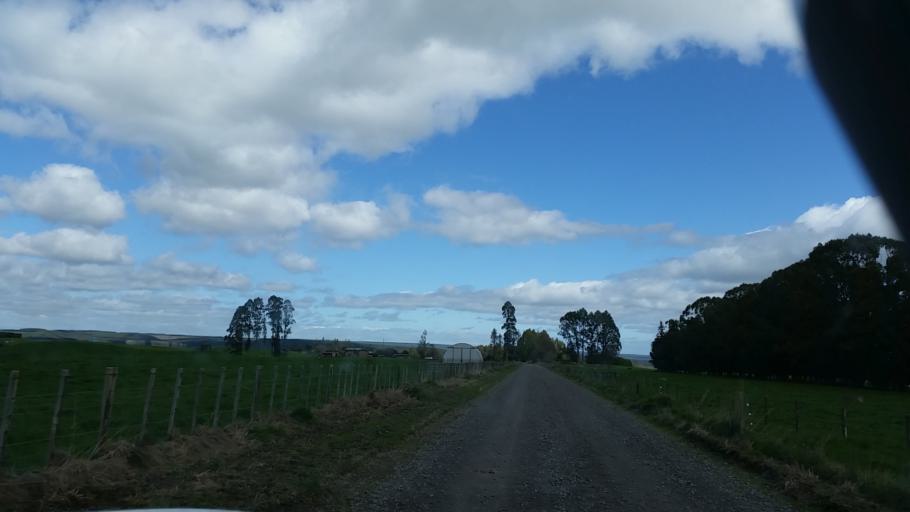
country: NZ
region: Bay of Plenty
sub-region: Whakatane District
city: Murupara
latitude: -38.4759
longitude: 176.4155
